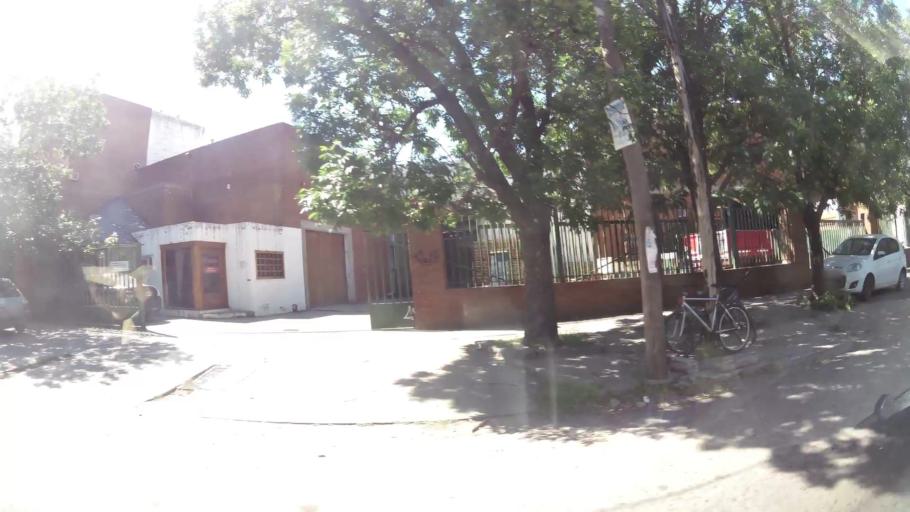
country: AR
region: Cordoba
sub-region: Departamento de Capital
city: Cordoba
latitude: -31.3678
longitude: -64.1732
